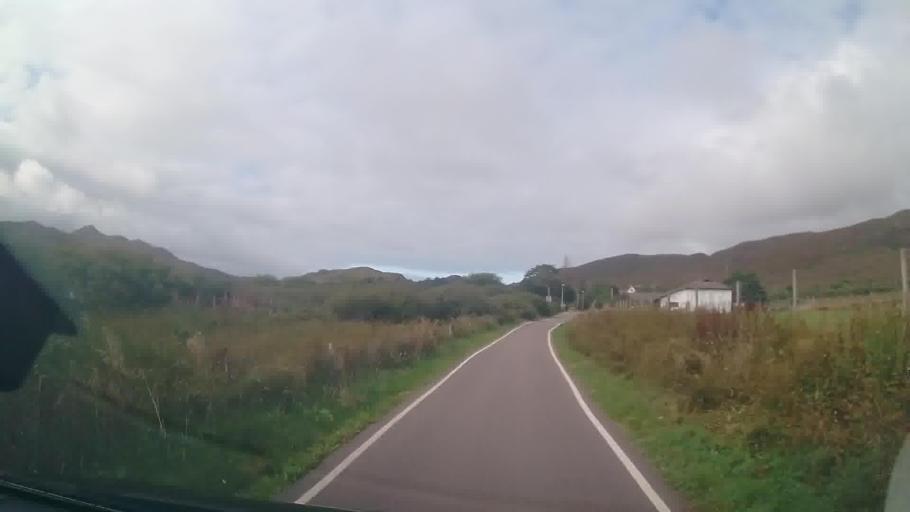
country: GB
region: Scotland
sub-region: Argyll and Bute
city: Isle Of Mull
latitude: 56.6954
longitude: -6.0996
